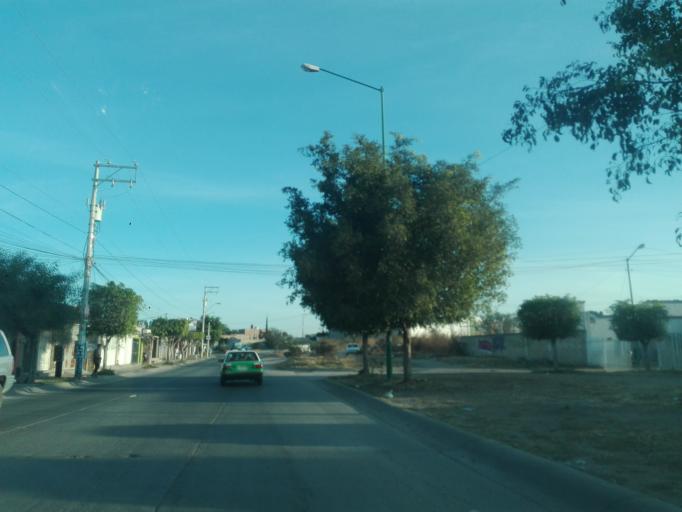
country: MX
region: Guanajuato
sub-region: Leon
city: San Jose de Duran (Los Troncoso)
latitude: 21.0781
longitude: -101.6379
